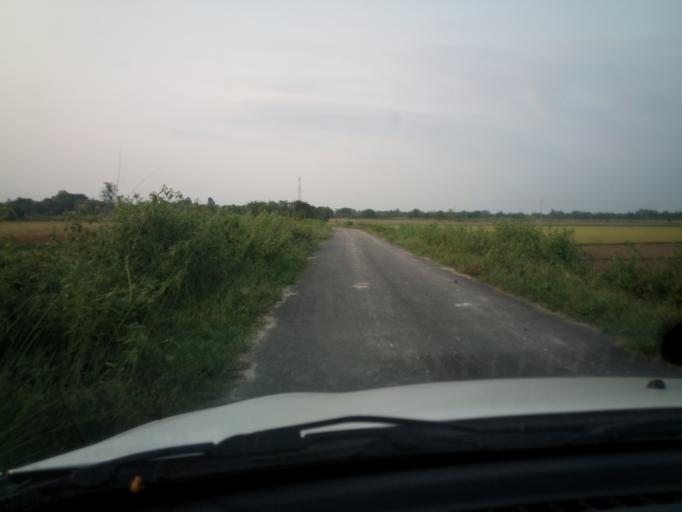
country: IN
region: Assam
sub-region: Udalguri
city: Udalguri
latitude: 26.6767
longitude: 92.1093
